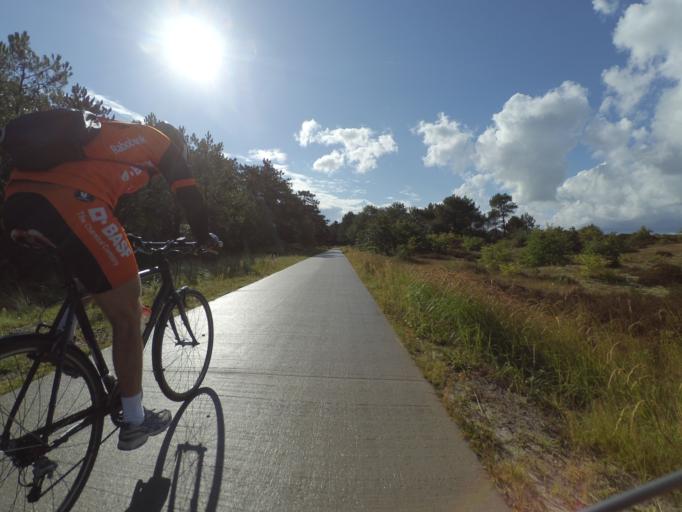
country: NL
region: North Holland
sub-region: Gemeente Bergen
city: Egmond aan Zee
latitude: 52.7007
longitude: 4.6701
